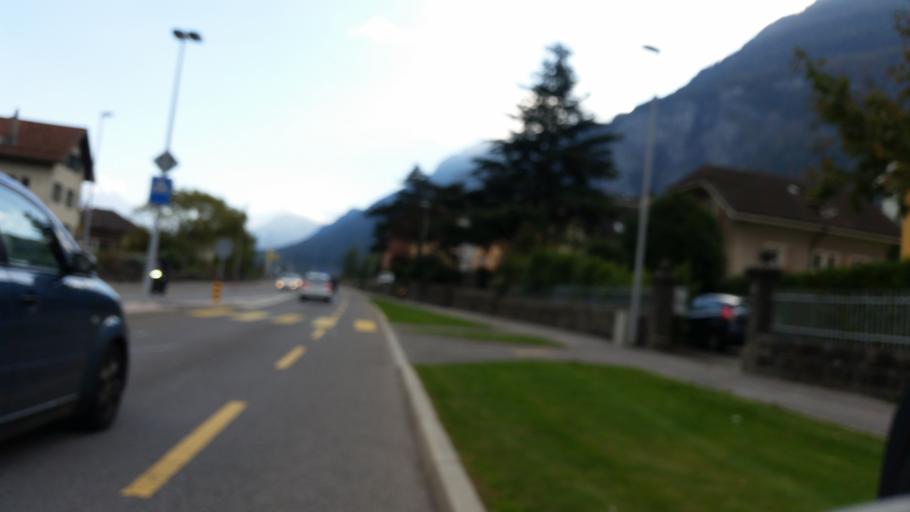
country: CH
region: Valais
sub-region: Saint-Maurice District
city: Saint-Maurice
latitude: 46.2113
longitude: 7.0058
